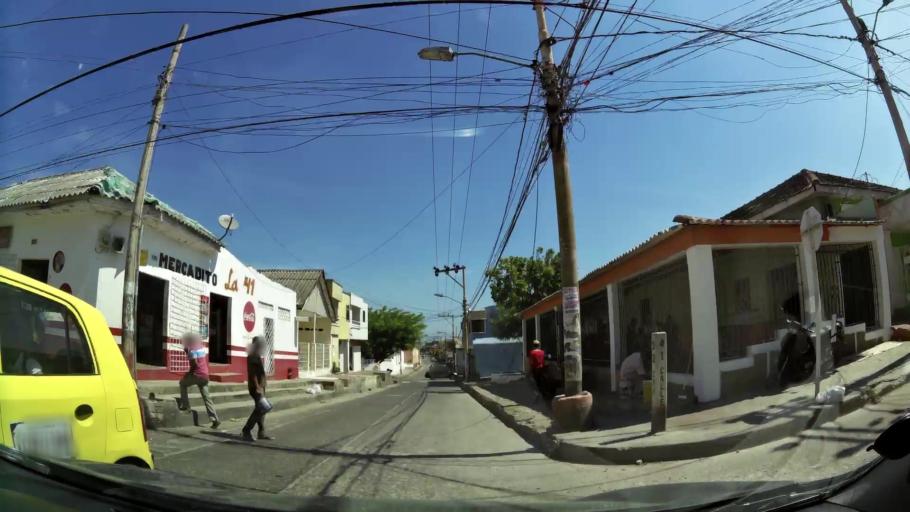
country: CO
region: Atlantico
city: Barranquilla
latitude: 10.9738
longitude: -74.7849
